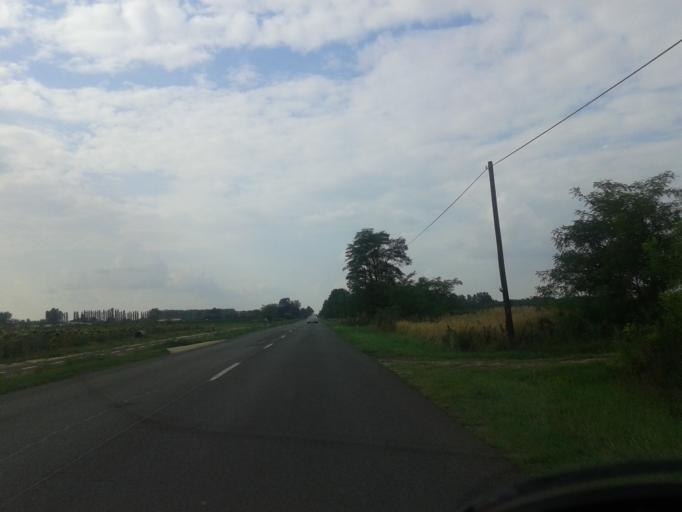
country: HU
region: Bacs-Kiskun
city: Akaszto
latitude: 46.6721
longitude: 19.2242
